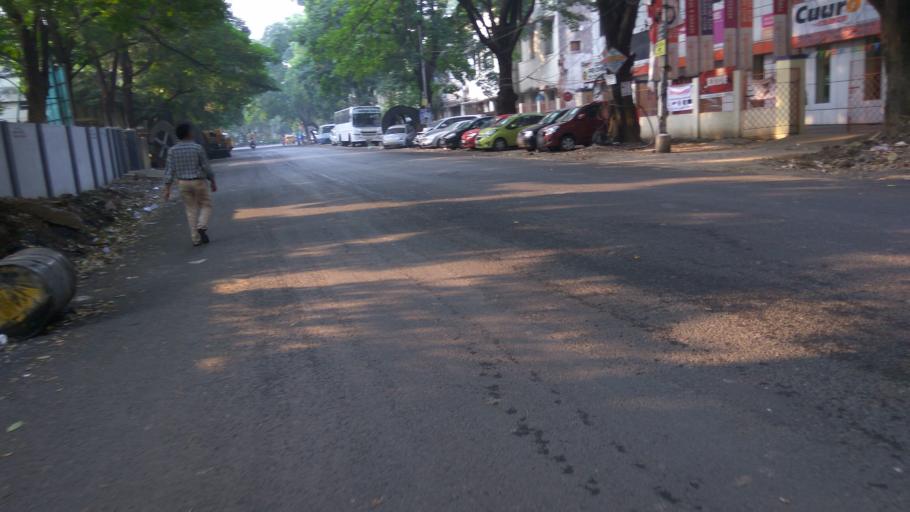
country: IN
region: Tamil Nadu
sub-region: Kancheepuram
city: Alandur
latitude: 13.0116
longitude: 80.2098
